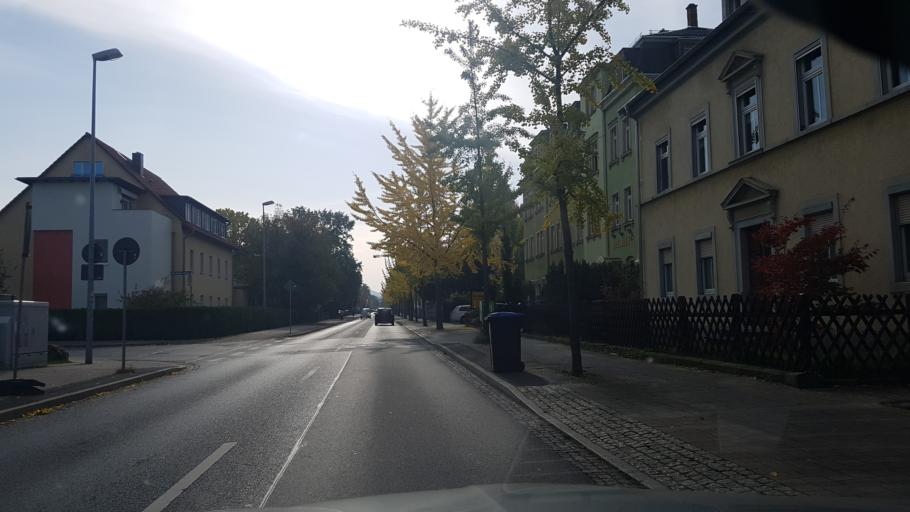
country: DE
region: Saxony
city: Pirna
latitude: 50.9520
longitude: 13.9403
